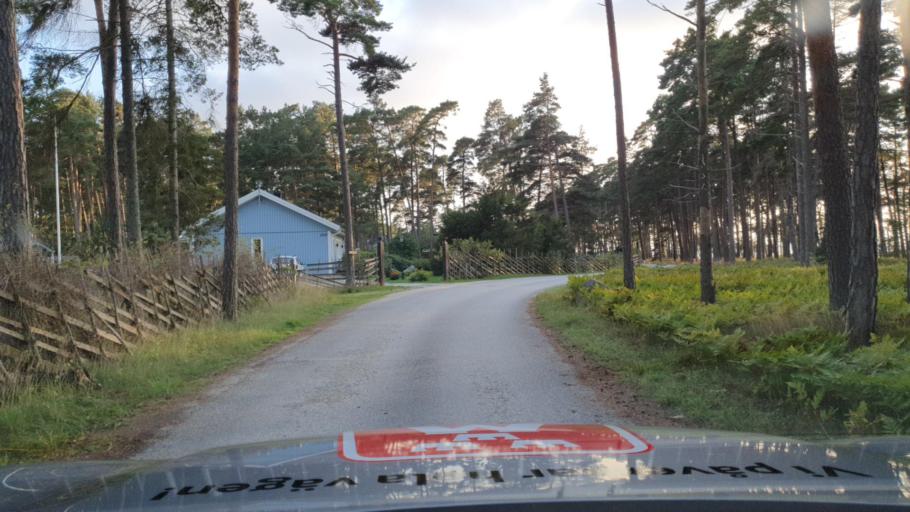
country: SE
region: Gotland
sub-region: Gotland
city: Klintehamn
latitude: 57.3135
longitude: 18.1583
